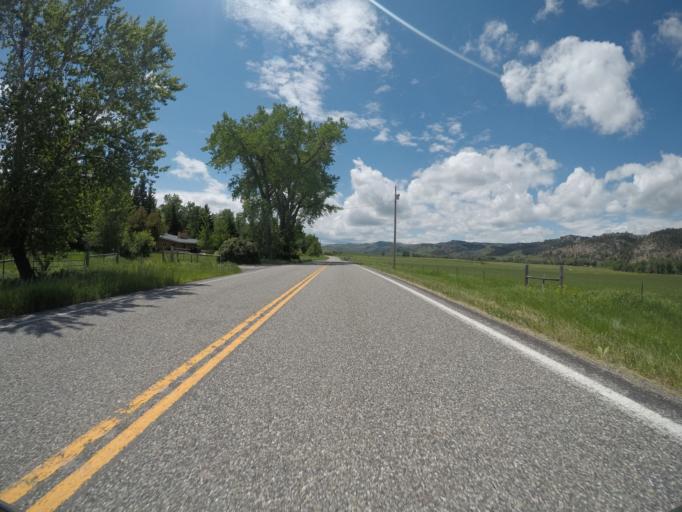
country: US
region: Montana
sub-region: Sweet Grass County
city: Big Timber
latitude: 45.6949
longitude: -110.0337
